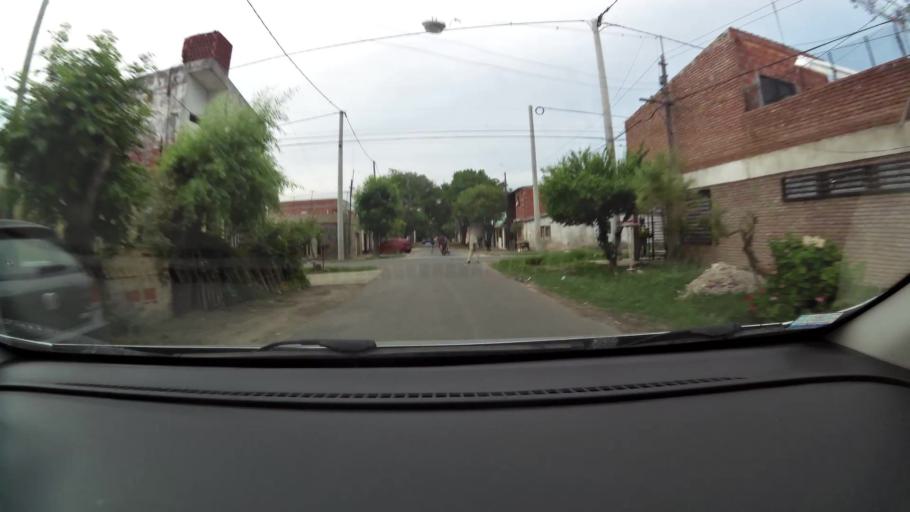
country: AR
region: Santa Fe
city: Granadero Baigorria
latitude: -32.8861
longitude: -60.7058
